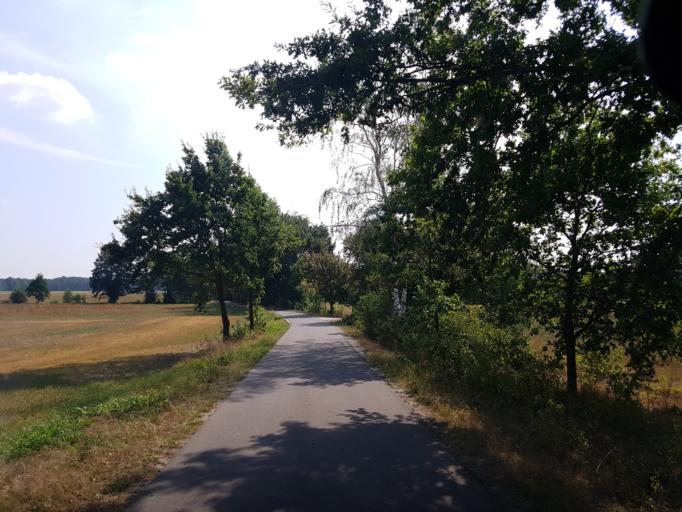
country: DE
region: Brandenburg
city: Finsterwalde
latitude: 51.6638
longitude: 13.7425
